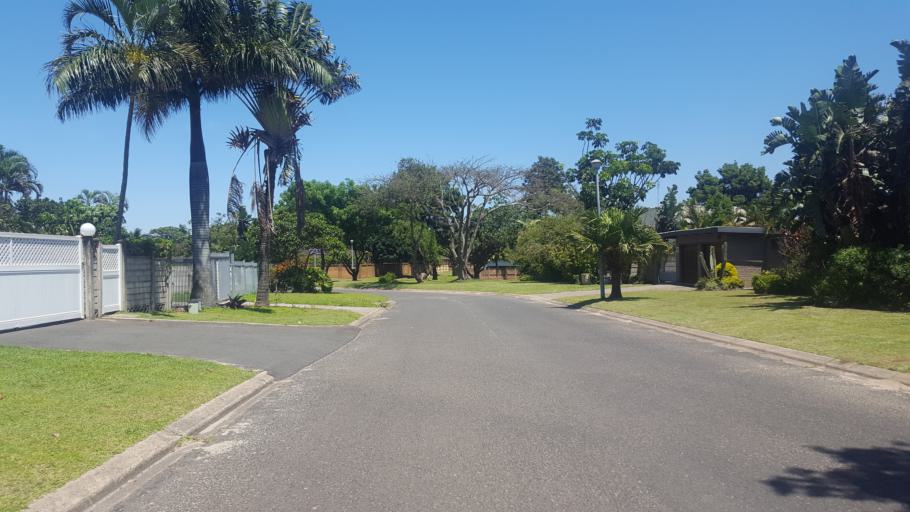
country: ZA
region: KwaZulu-Natal
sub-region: uThungulu District Municipality
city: Richards Bay
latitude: -28.7654
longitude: 32.0631
